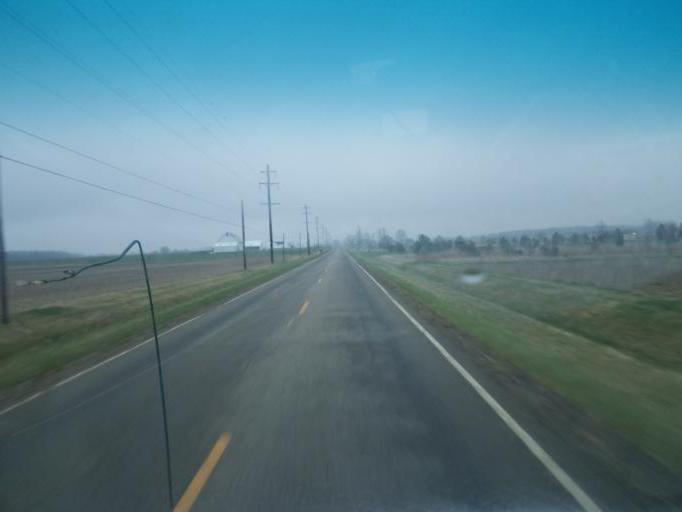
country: US
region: Ohio
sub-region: Defiance County
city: Hicksville
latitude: 41.3480
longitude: -84.7670
